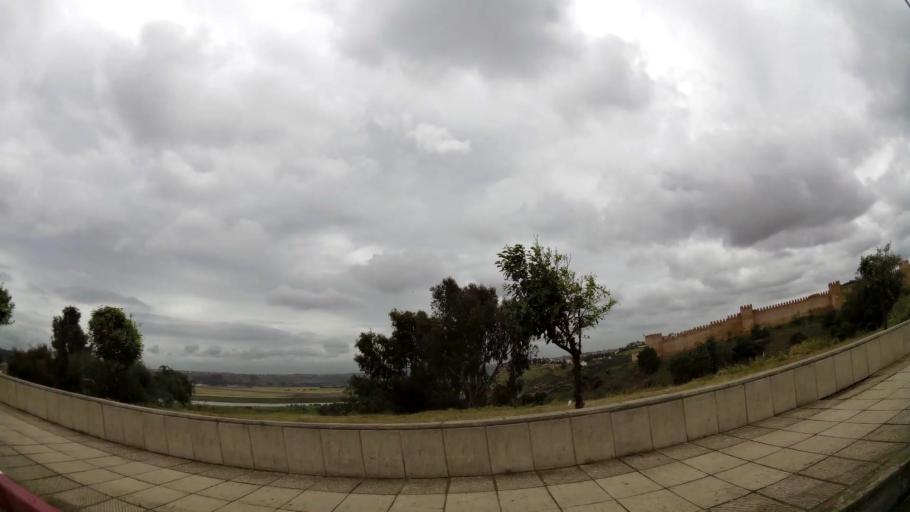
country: MA
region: Rabat-Sale-Zemmour-Zaer
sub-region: Rabat
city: Rabat
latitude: 34.0099
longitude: -6.8217
